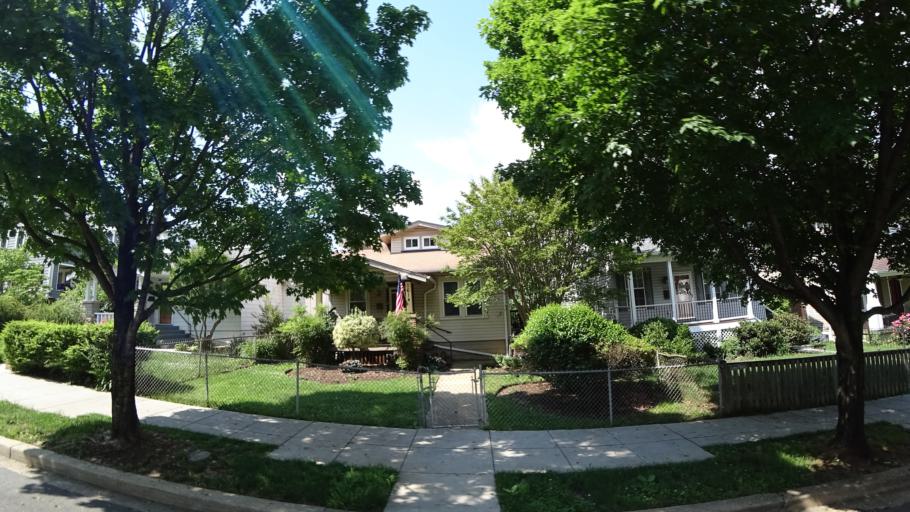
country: US
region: Maryland
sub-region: Prince George's County
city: Mount Rainier
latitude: 38.9340
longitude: -76.9820
